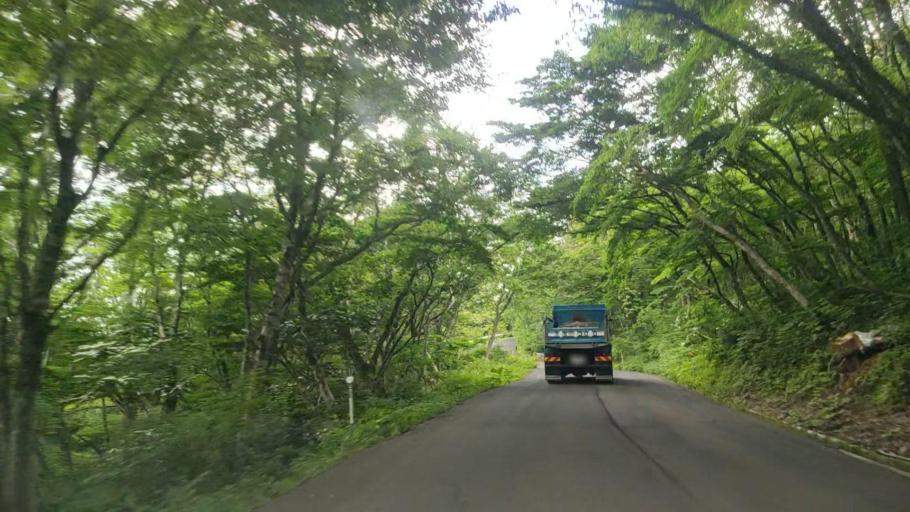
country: JP
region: Tottori
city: Yonago
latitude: 35.3818
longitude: 133.5232
